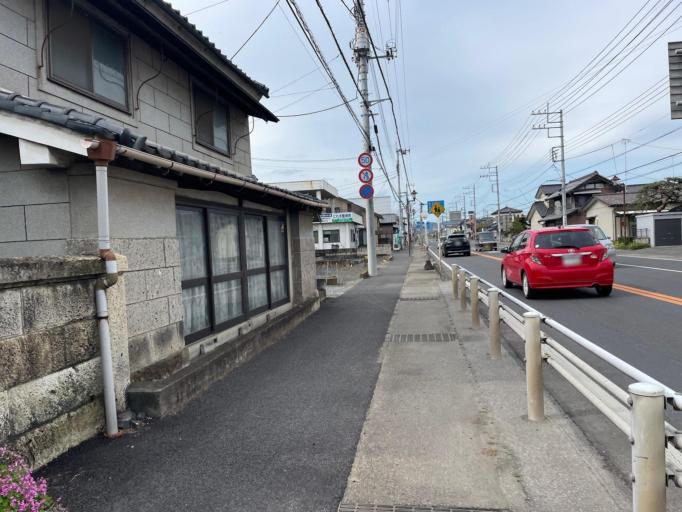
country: JP
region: Tochigi
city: Kanuma
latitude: 36.5040
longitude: 139.7512
